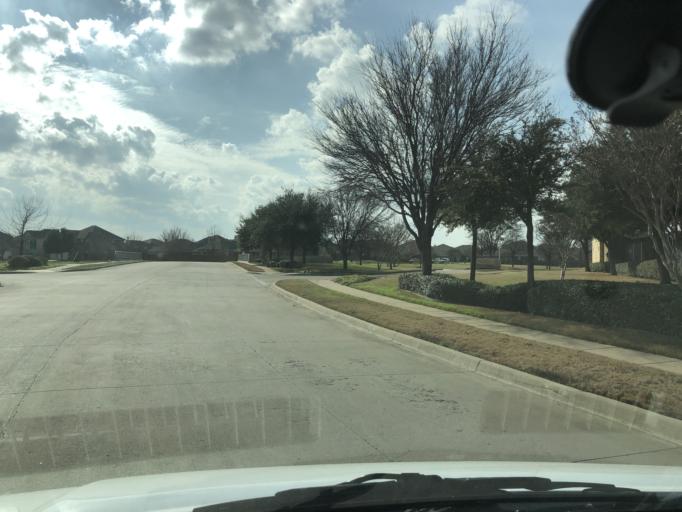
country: US
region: Texas
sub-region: Tarrant County
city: Haslet
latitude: 32.9190
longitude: -97.3662
